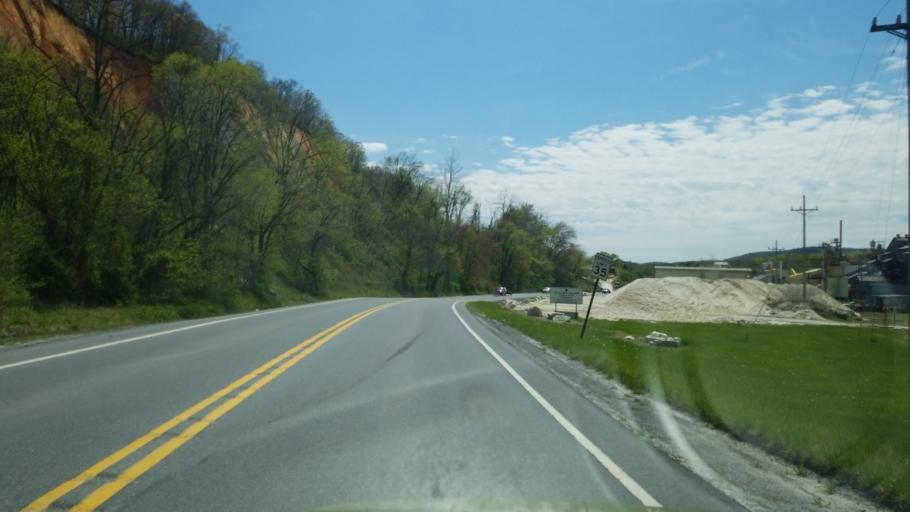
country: US
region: Pennsylvania
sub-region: Huntingdon County
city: Mount Union
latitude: 40.4106
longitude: -77.9337
